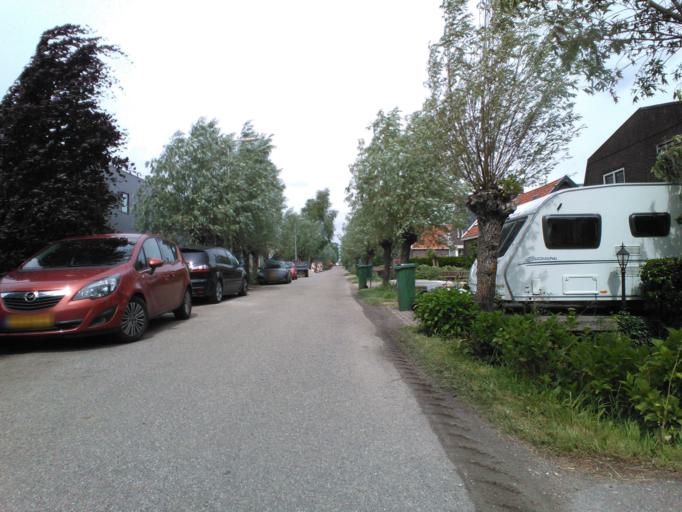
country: NL
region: South Holland
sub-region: Gemeente Vlist
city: Haastrecht
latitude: 51.9624
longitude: 4.7779
